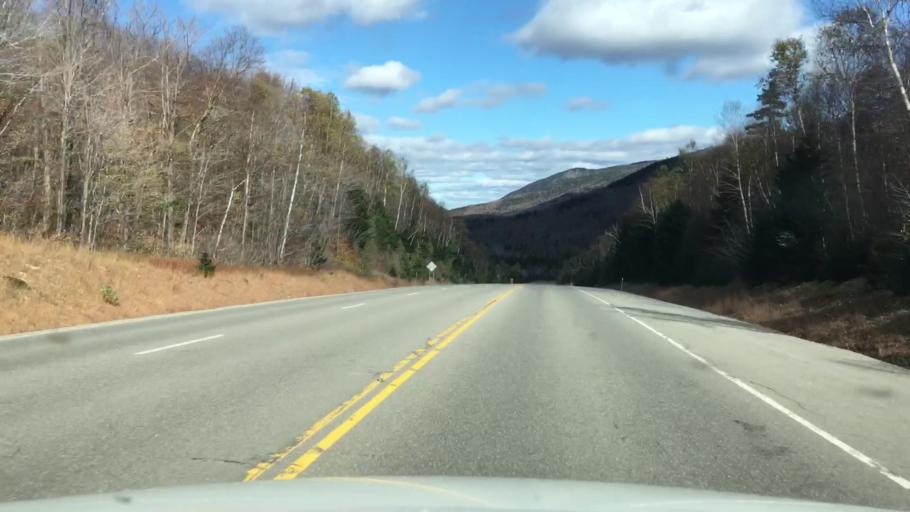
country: US
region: New Hampshire
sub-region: Coos County
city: Gorham
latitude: 44.2671
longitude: -71.2386
